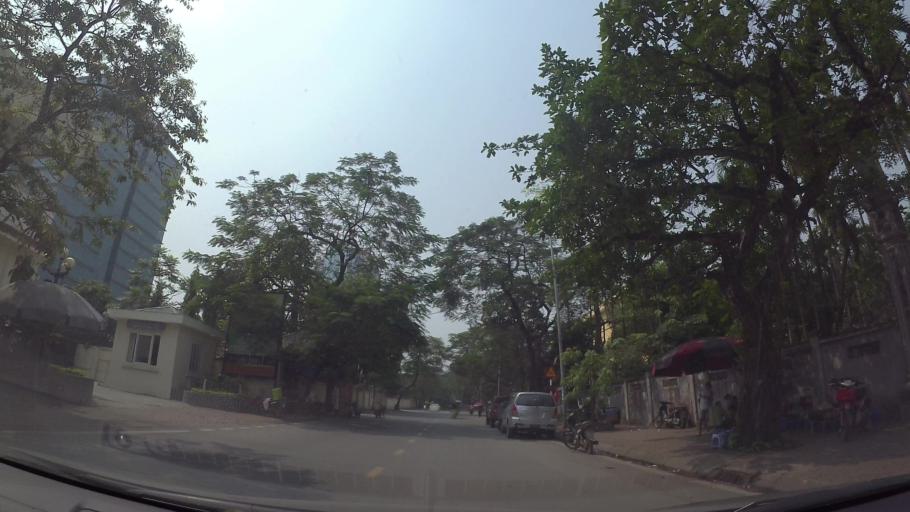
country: VN
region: Ha Noi
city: Dong Da
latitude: 21.0319
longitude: 105.8271
